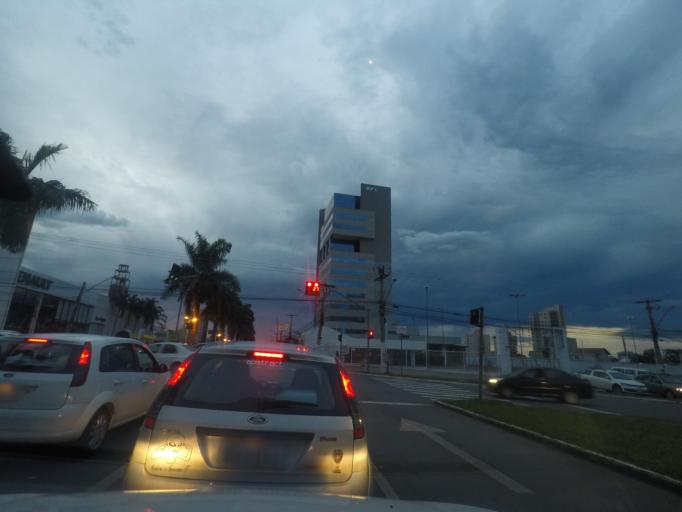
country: BR
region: Goias
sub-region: Goiania
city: Goiania
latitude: -16.7142
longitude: -49.2744
